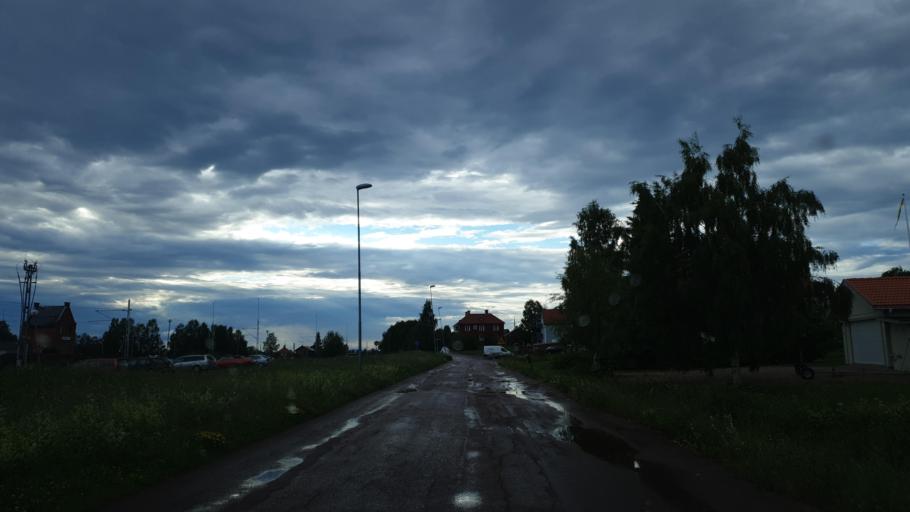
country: SE
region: Dalarna
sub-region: Mora Kommun
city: Mora
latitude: 61.0021
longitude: 14.5819
